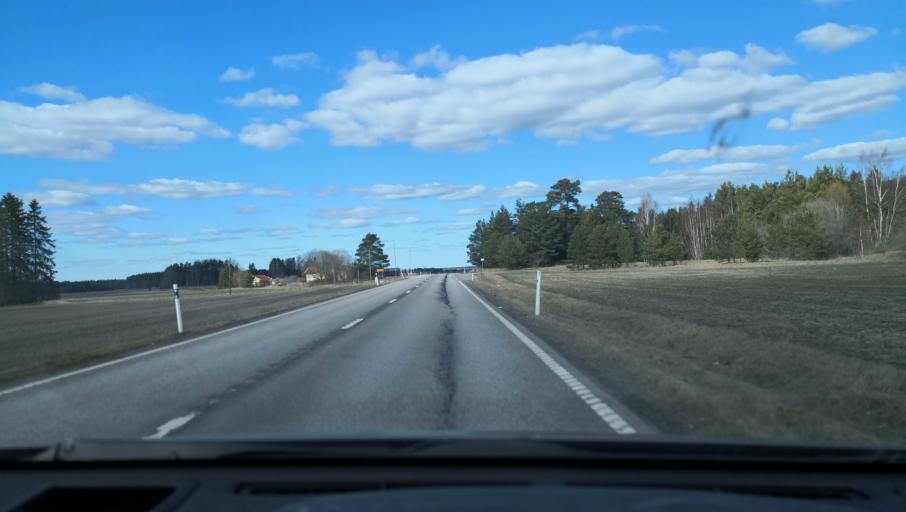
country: SE
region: Vaestmanland
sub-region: Sala Kommun
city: Sala
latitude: 59.8712
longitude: 16.6277
